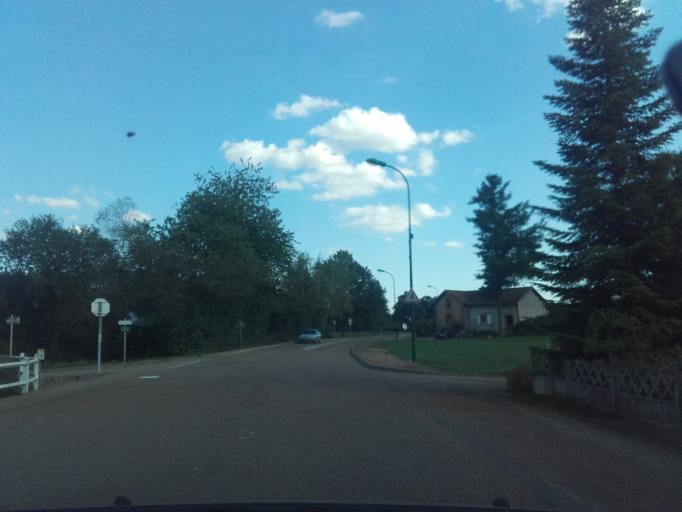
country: FR
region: Bourgogne
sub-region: Departement de Saone-et-Loire
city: Epinac
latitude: 47.0050
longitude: 4.4743
